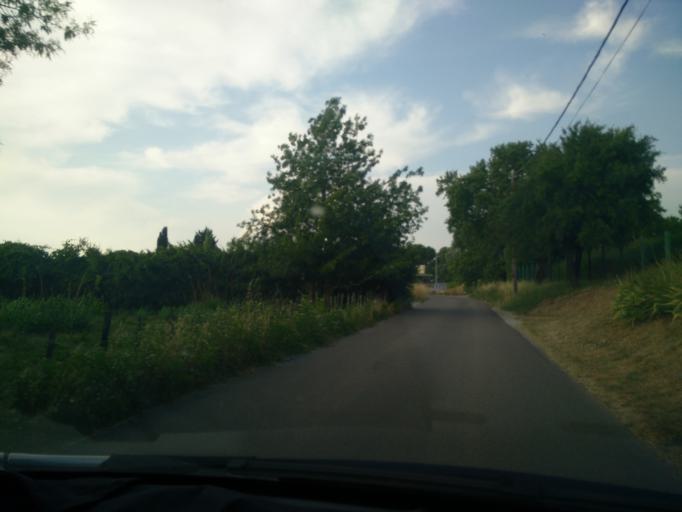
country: FR
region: Languedoc-Roussillon
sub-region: Departement du Gard
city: Gallargues-le-Montueux
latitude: 43.6912
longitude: 4.1633
